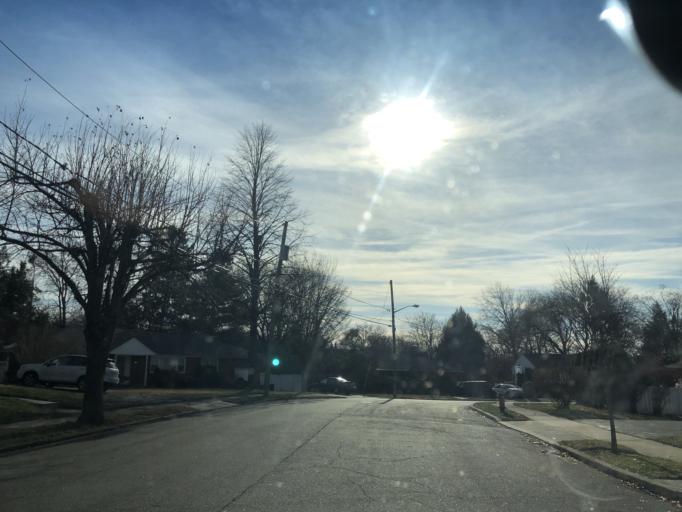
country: US
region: New Jersey
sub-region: Bergen County
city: Fair Lawn
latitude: 40.9256
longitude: -74.1303
